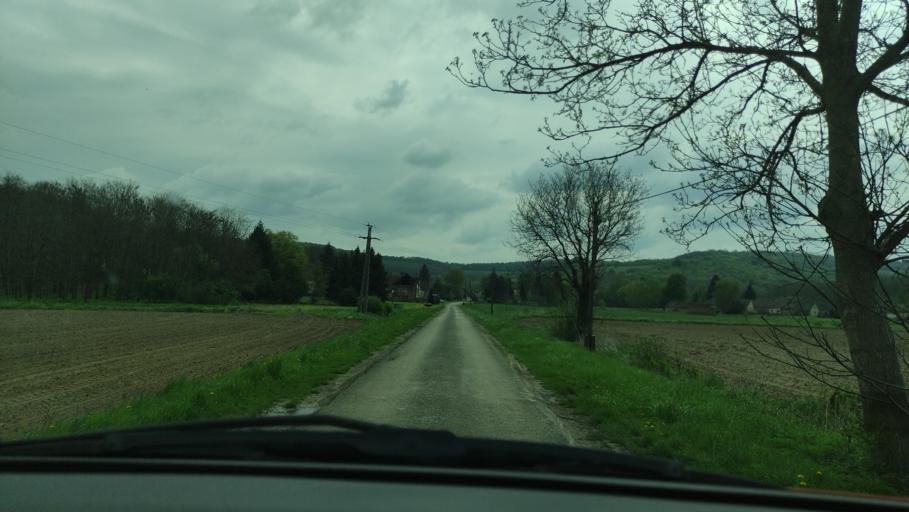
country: HU
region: Baranya
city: Sasd
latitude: 46.2831
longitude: 18.1378
